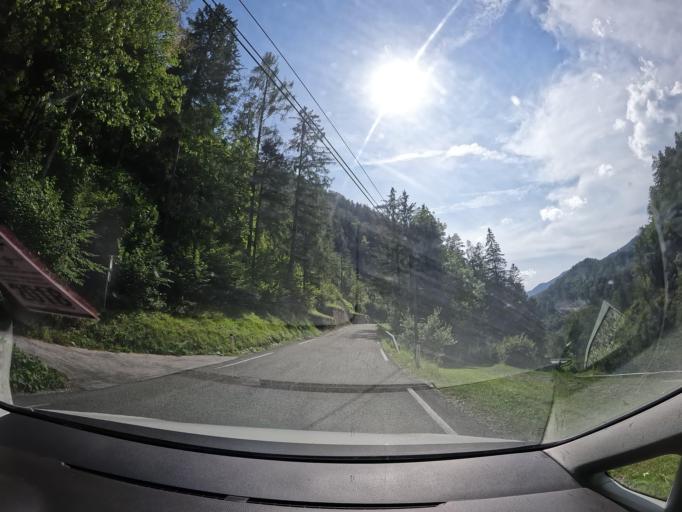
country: AT
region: Carinthia
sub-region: Politischer Bezirk Klagenfurt Land
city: Ludmannsdorf
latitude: 46.5124
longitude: 14.0997
